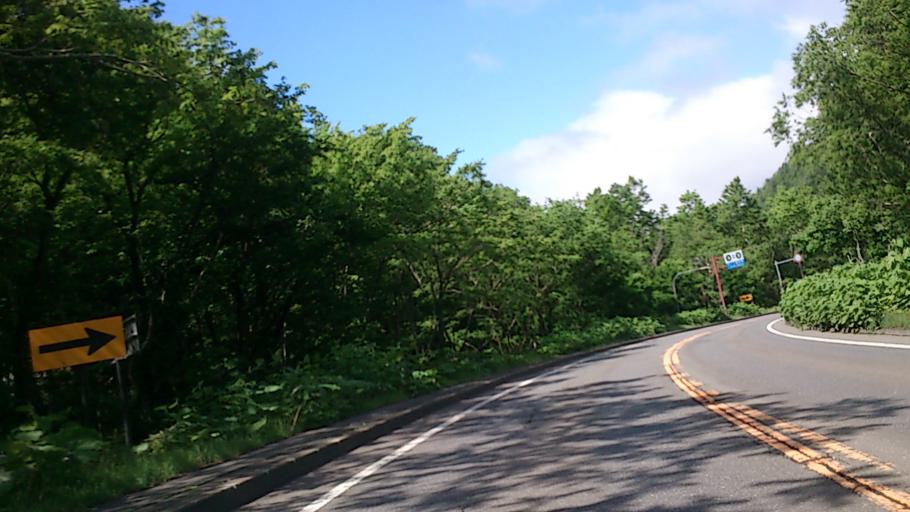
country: JP
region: Hokkaido
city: Shiraoi
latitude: 42.7173
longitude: 141.2199
